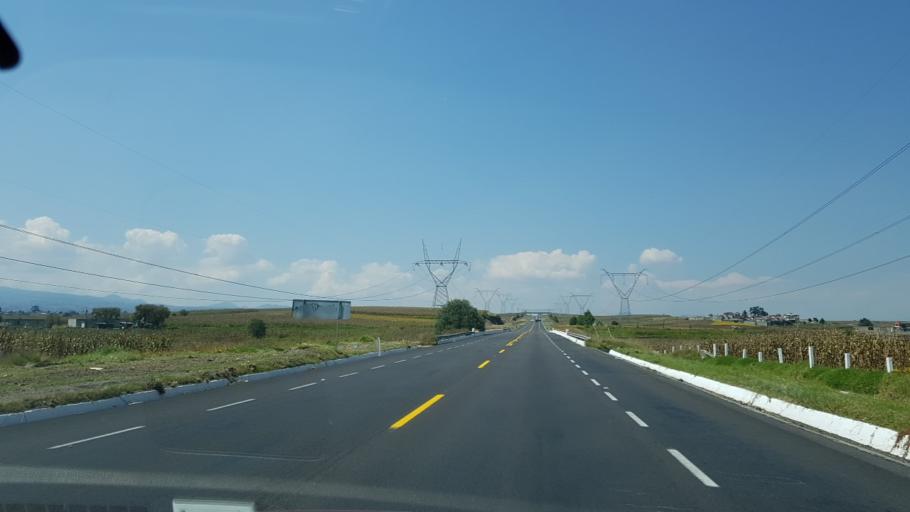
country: MX
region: Mexico
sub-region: Almoloya de Juarez
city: Conjunto Habitacional Ecologico SUTEYM
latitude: 19.3846
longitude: -99.7693
